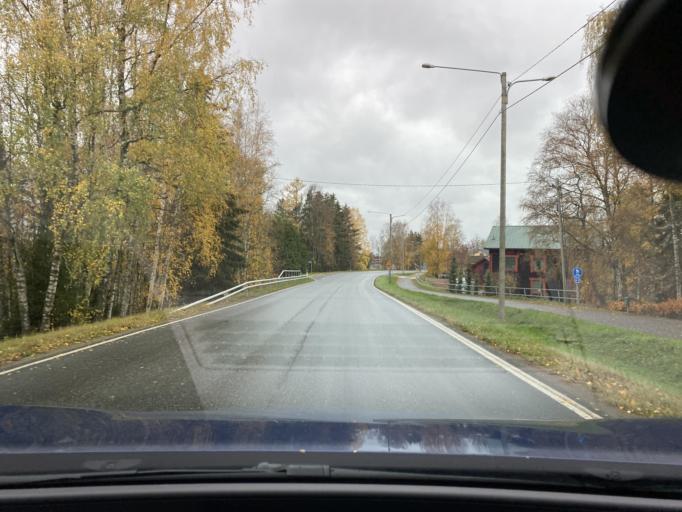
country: FI
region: Satakunta
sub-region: Pori
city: Kokemaeki
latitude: 61.2570
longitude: 22.3708
